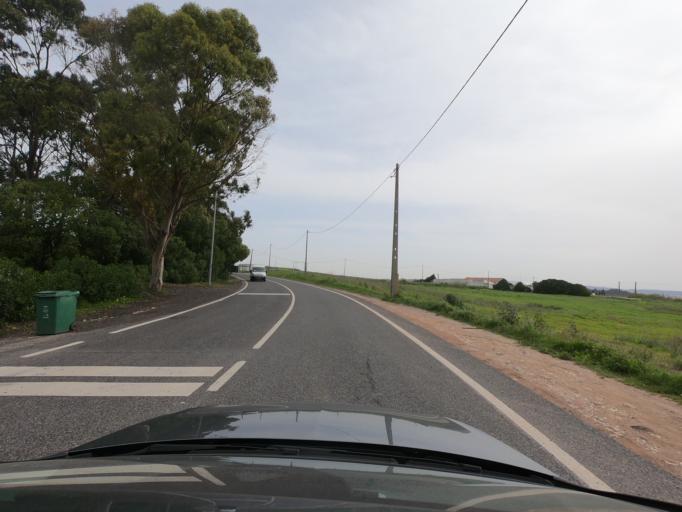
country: PT
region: Lisbon
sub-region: Oeiras
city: Porto Salvo
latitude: 38.7213
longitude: -9.2913
